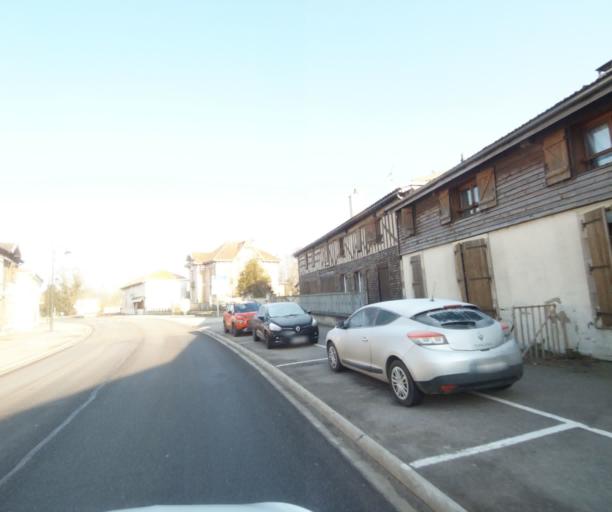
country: FR
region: Champagne-Ardenne
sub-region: Departement de la Haute-Marne
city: Montier-en-Der
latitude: 48.4723
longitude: 4.7648
